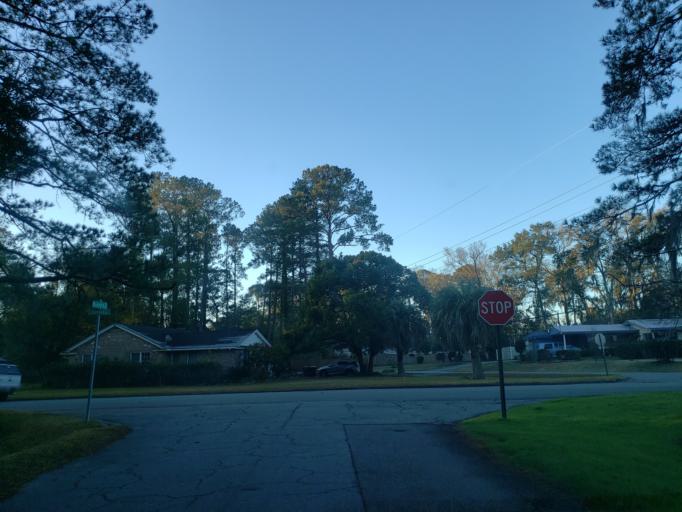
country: US
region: Georgia
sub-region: Chatham County
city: Thunderbolt
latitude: 32.0171
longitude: -81.0837
